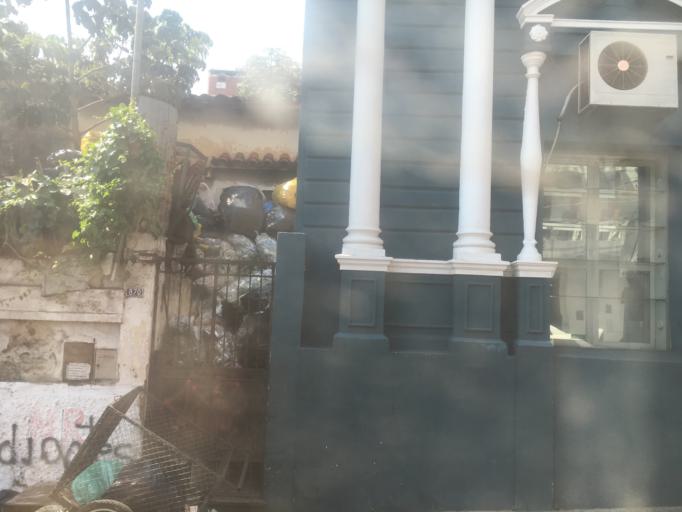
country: PY
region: Asuncion
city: Asuncion
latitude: -25.2812
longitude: -57.6410
